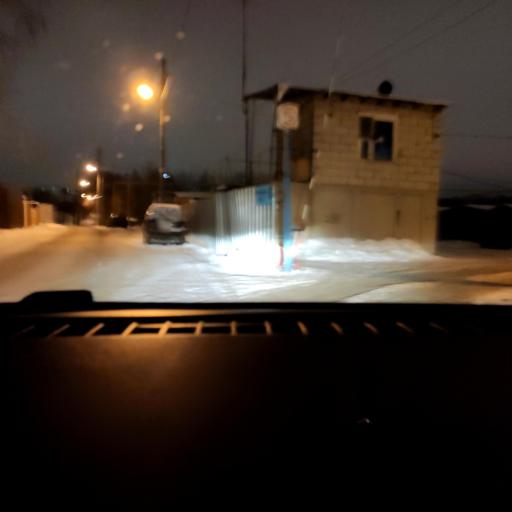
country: RU
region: Samara
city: Samara
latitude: 53.2208
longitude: 50.1687
